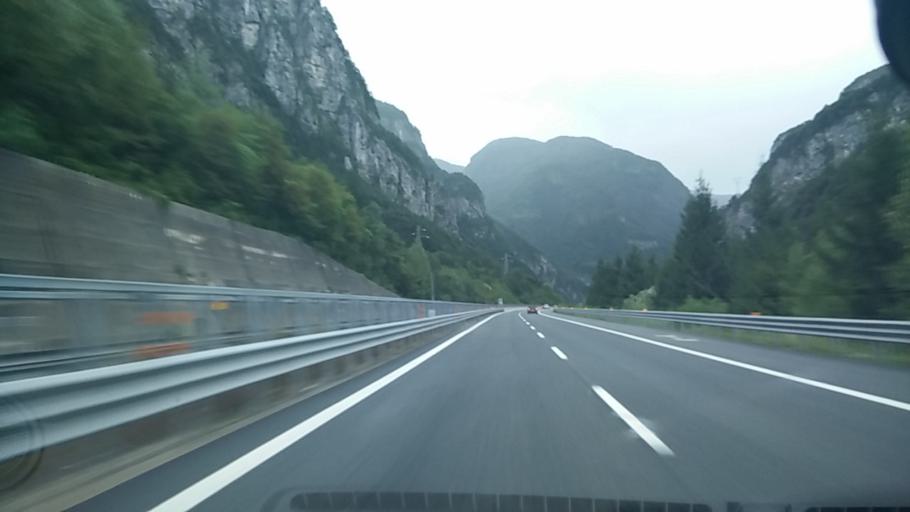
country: IT
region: Friuli Venezia Giulia
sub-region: Provincia di Udine
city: Dogna
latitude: 46.4340
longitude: 13.3135
